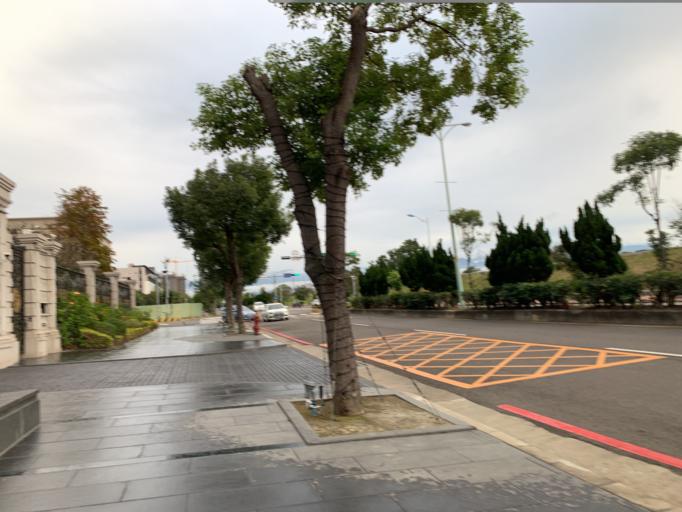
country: TW
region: Taiwan
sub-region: Hsinchu
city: Zhubei
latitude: 24.8148
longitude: 121.0158
